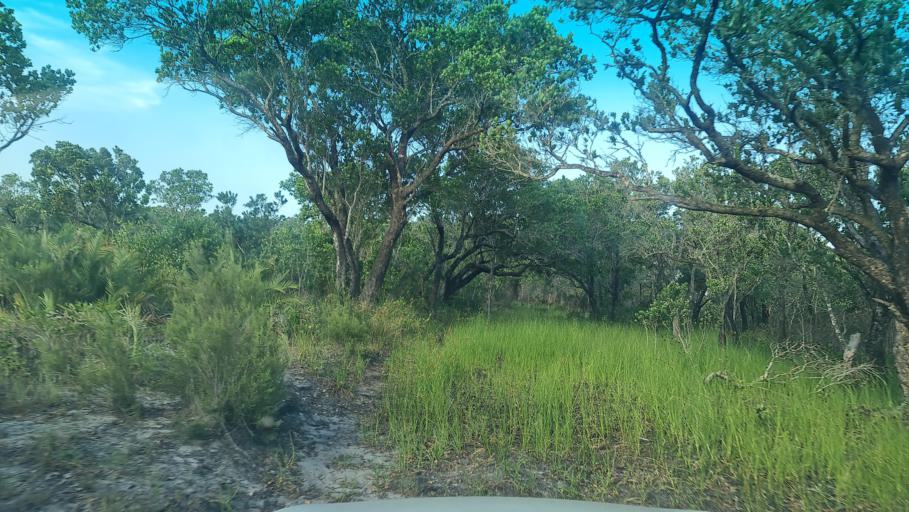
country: MZ
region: Gaza
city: Macia
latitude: -25.2259
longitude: 33.0247
